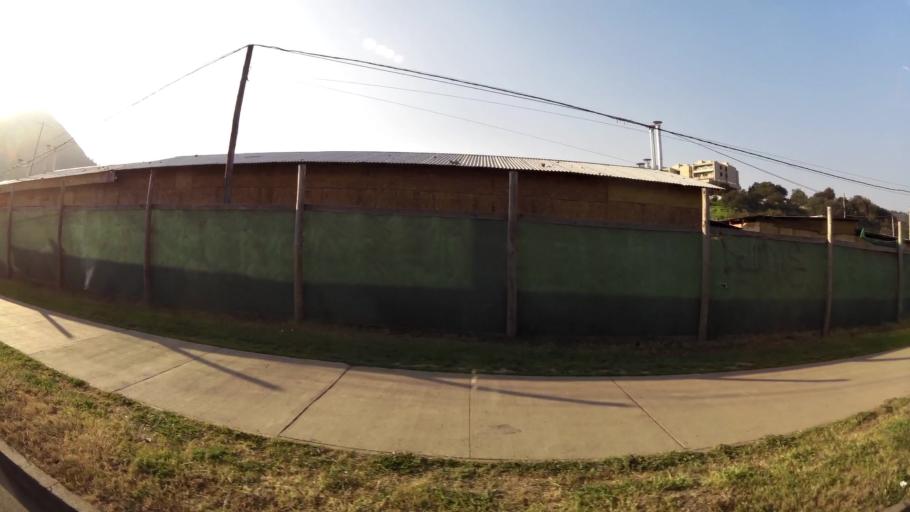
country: CL
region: Santiago Metropolitan
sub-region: Provincia de Santiago
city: Villa Presidente Frei, Nunoa, Santiago, Chile
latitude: -33.3548
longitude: -70.5425
